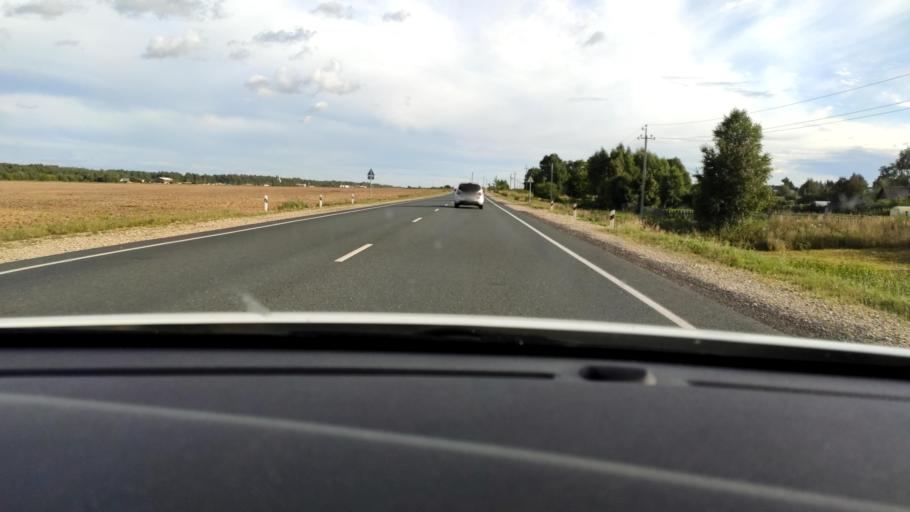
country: RU
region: Mariy-El
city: Suslonger
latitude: 56.2226
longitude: 48.2351
